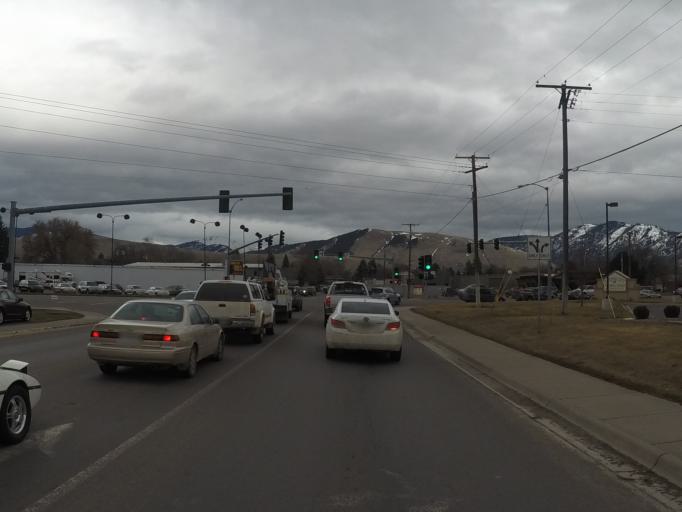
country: US
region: Montana
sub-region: Missoula County
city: Missoula
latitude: 46.8806
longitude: -114.0226
